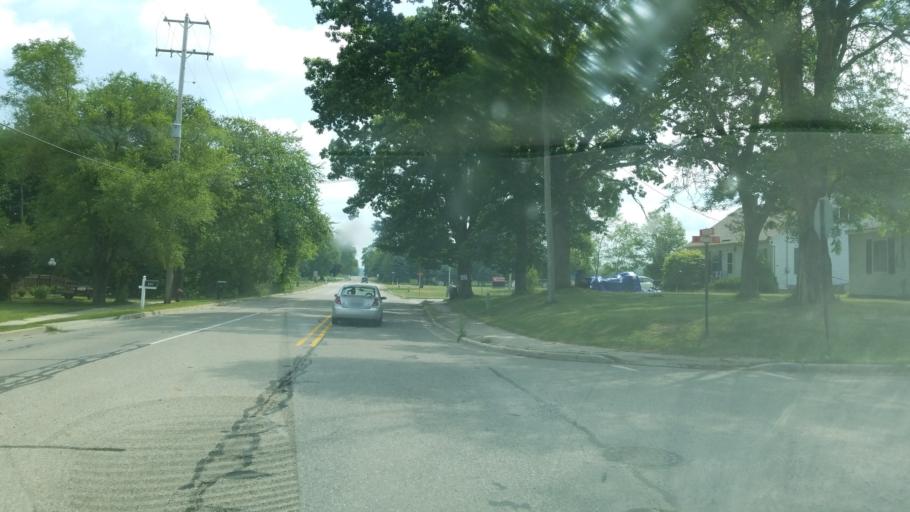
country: US
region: Michigan
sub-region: Kent County
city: Cedar Springs
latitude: 43.2200
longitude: -85.5414
